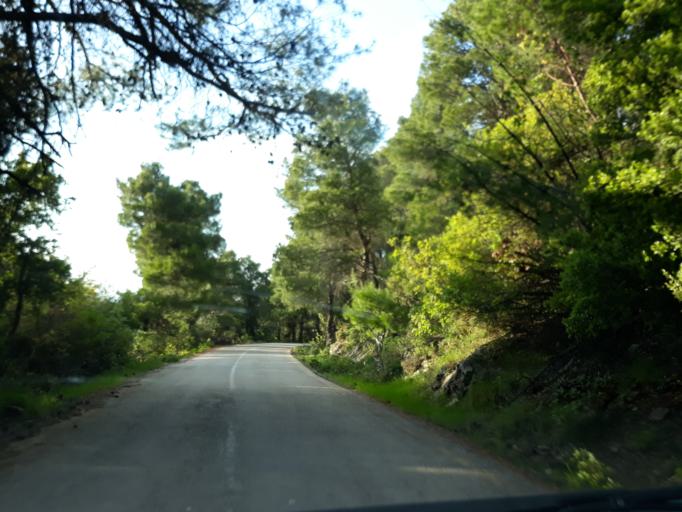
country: GR
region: Attica
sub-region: Nomarchia Anatolikis Attikis
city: Afidnes
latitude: 38.2203
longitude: 23.7805
